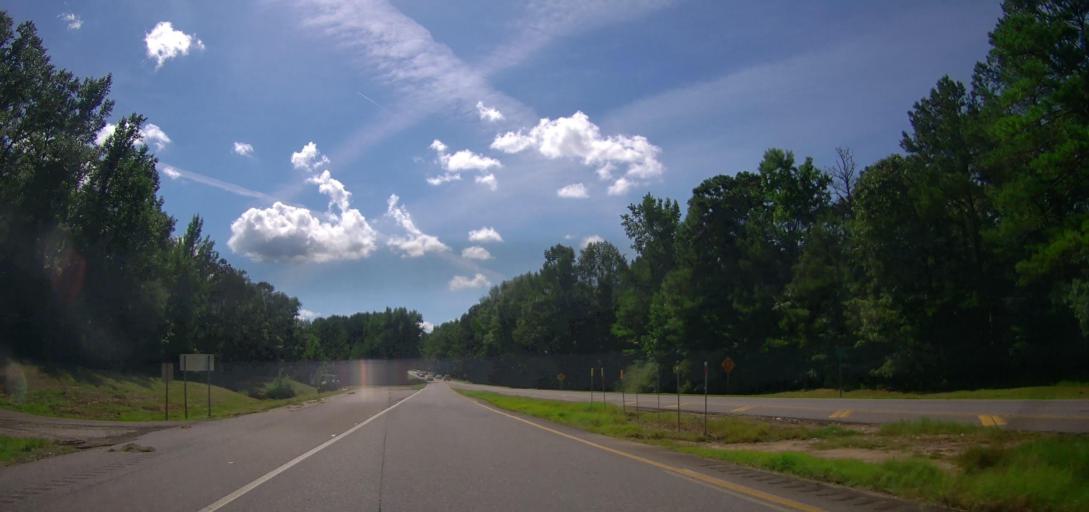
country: US
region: Alabama
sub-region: Pickens County
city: Gordo
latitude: 33.2841
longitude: -87.8376
